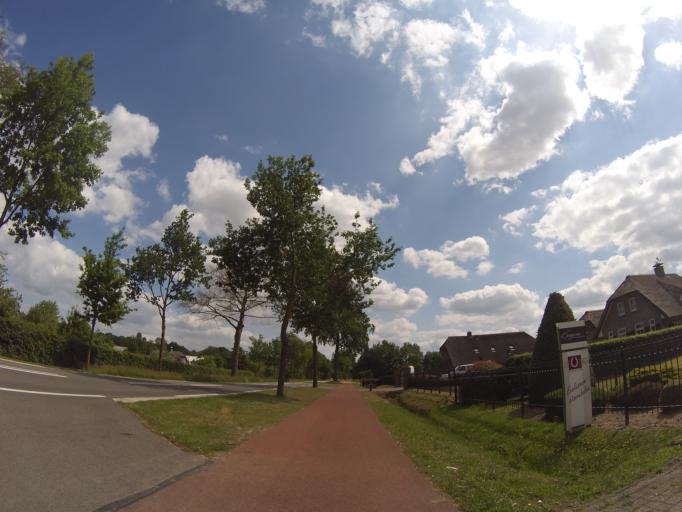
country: NL
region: Gelderland
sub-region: Gemeente Barneveld
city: Terschuur
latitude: 52.1682
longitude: 5.5474
